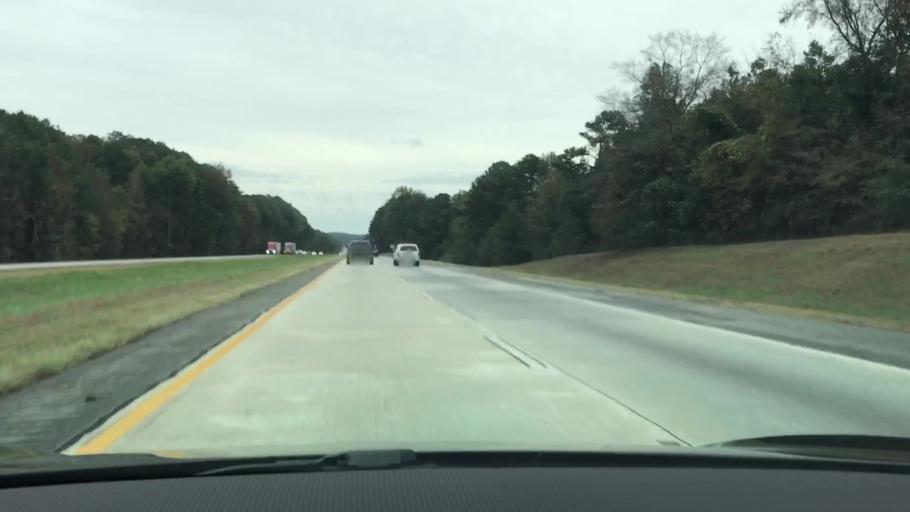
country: US
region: Georgia
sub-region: Greene County
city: Greensboro
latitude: 33.5478
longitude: -83.1656
